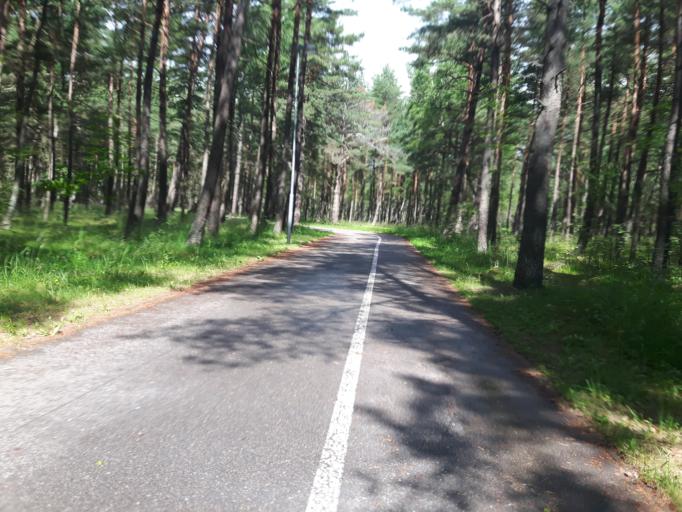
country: LT
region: Klaipedos apskritis
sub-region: Klaipeda
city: Klaipeda
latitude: 55.7594
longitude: 21.1028
